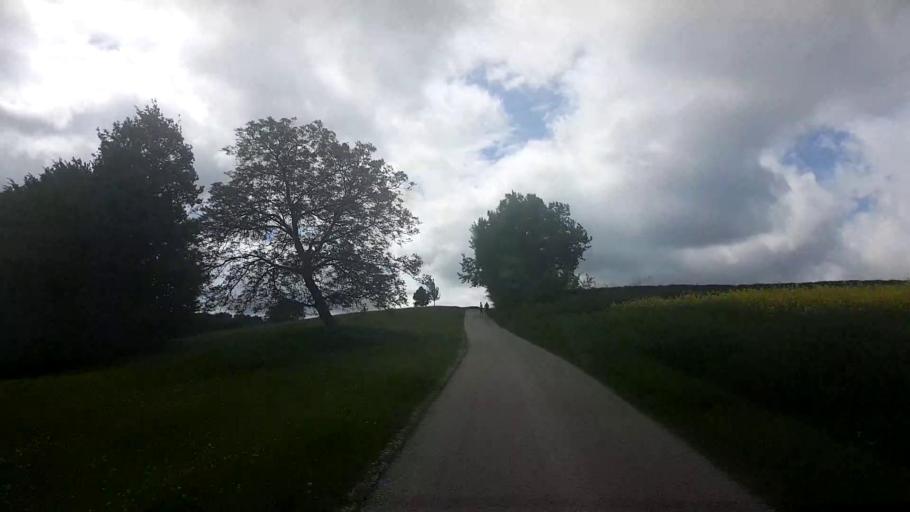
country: DE
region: Bavaria
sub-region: Upper Franconia
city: Bad Staffelstein
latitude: 50.1065
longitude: 11.0370
